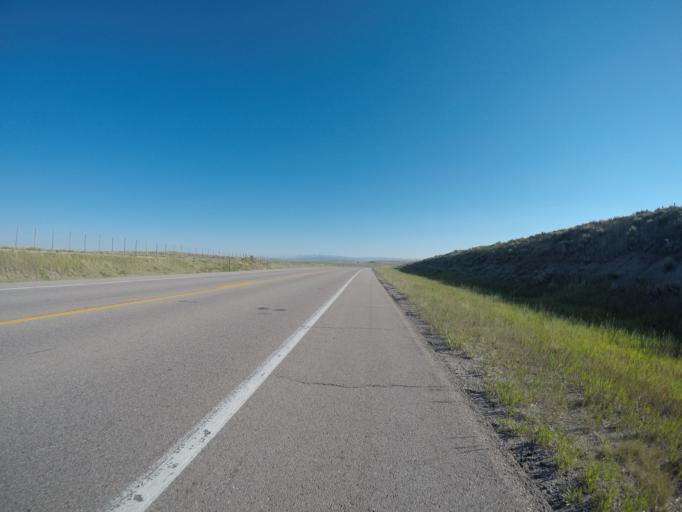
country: US
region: Wyoming
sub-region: Sublette County
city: Pinedale
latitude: 42.9214
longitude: -110.0804
